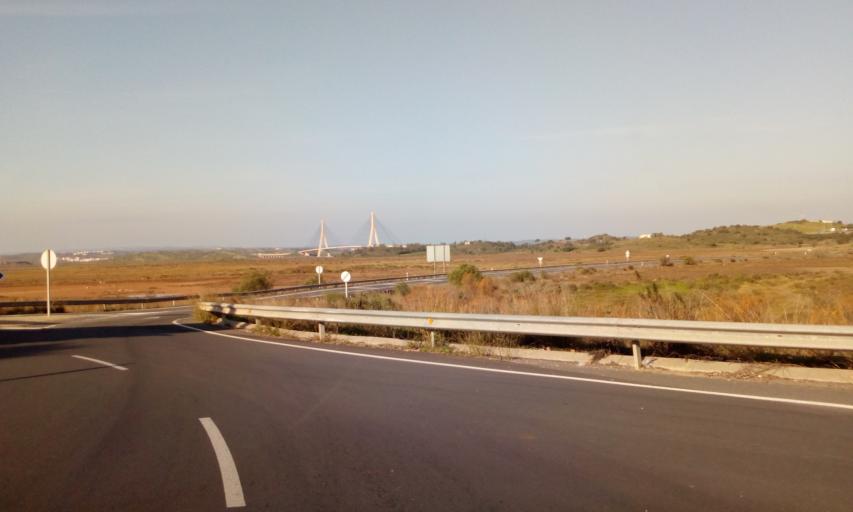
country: ES
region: Andalusia
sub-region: Provincia de Huelva
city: Ayamonte
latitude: 37.2317
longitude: -7.4020
